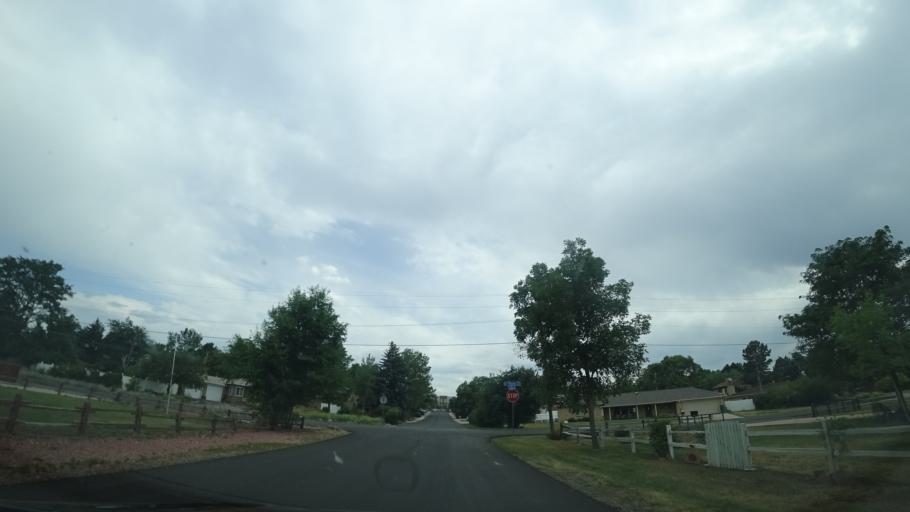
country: US
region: Colorado
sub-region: Jefferson County
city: Lakewood
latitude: 39.7151
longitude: -105.0862
